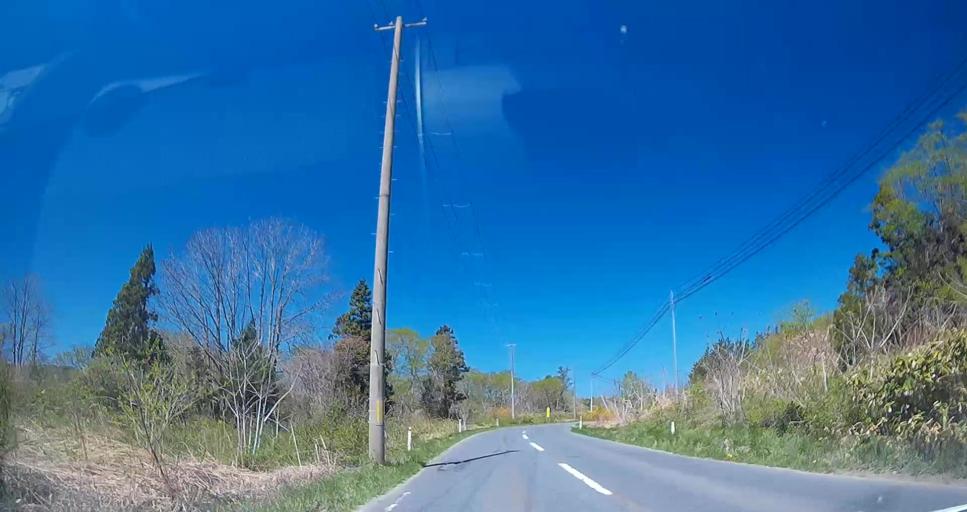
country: JP
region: Aomori
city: Misawa
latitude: 40.9281
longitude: 141.3767
